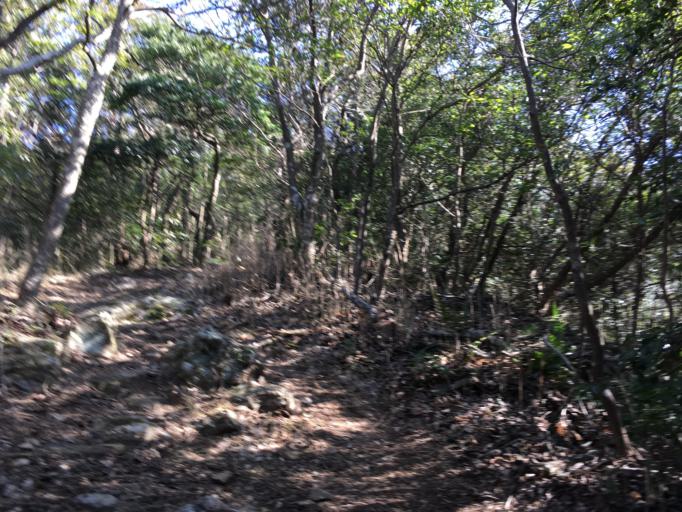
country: JP
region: Aichi
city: Toyohashi
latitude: 34.7365
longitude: 137.4421
